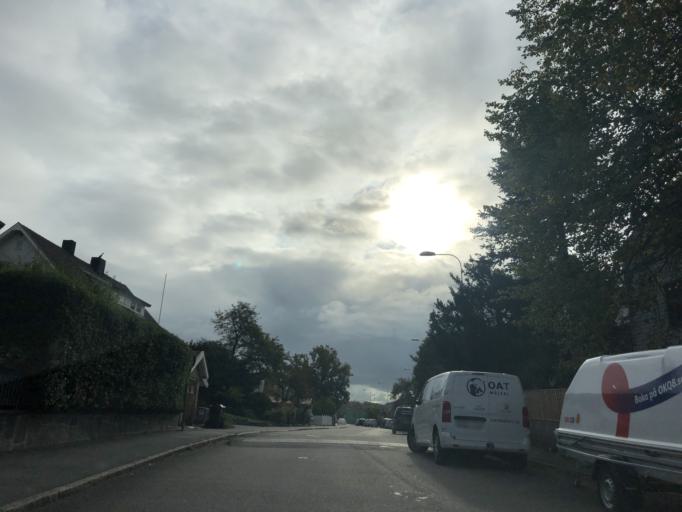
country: SE
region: Vaestra Goetaland
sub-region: Goteborg
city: Majorna
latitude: 57.6759
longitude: 11.8783
